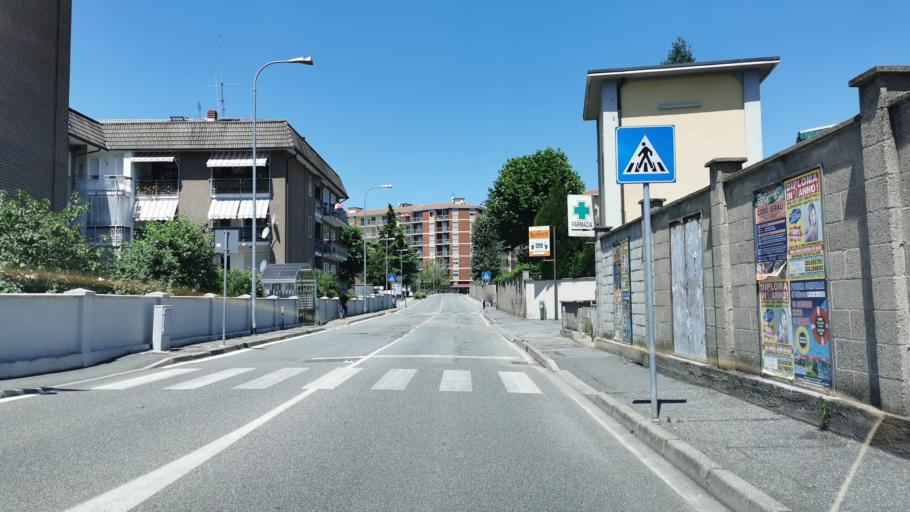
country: IT
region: Piedmont
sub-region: Provincia di Torino
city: Brandizzo
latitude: 45.1781
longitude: 7.8359
